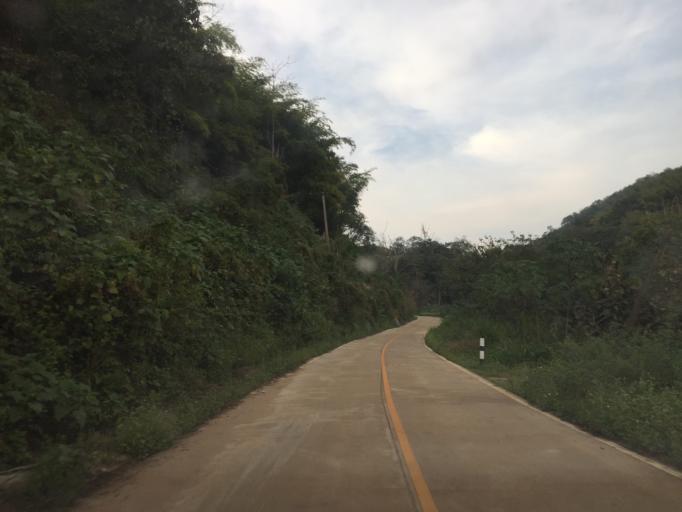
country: TH
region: Chiang Mai
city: Samoeng
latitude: 18.9907
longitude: 98.7077
